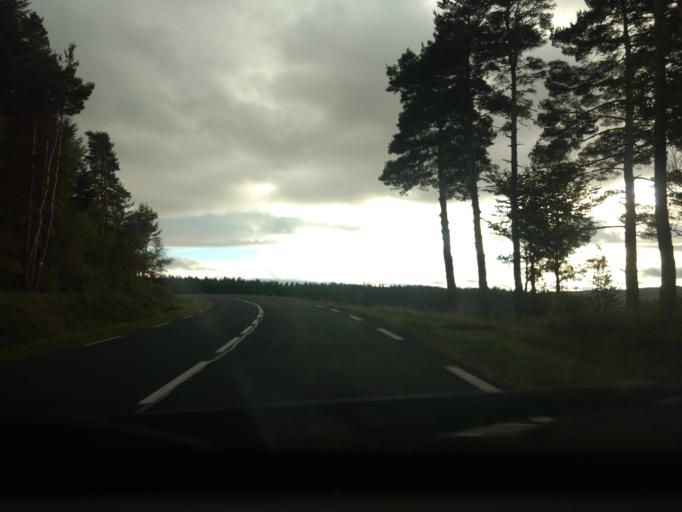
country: FR
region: Auvergne
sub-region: Departement du Cantal
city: Chaudes-Aigues
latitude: 44.8226
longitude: 2.9769
